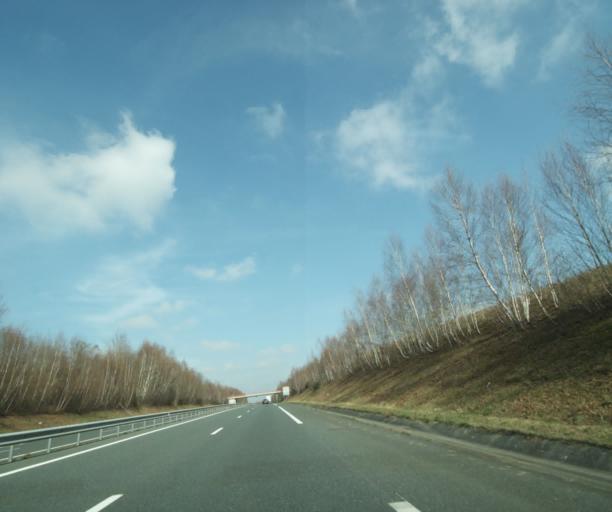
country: FR
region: Limousin
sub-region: Departement de la Haute-Vienne
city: Saint-Sulpice-les-Feuilles
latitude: 46.3681
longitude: 1.4394
